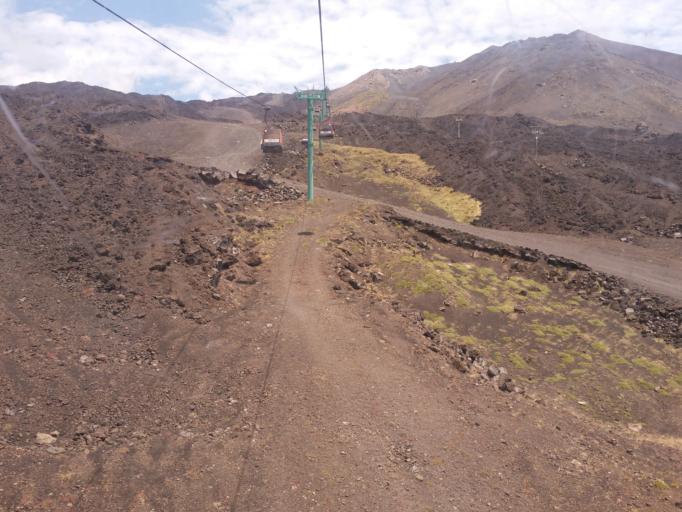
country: IT
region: Sicily
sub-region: Catania
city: Ragalna
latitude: 37.7026
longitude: 14.9991
